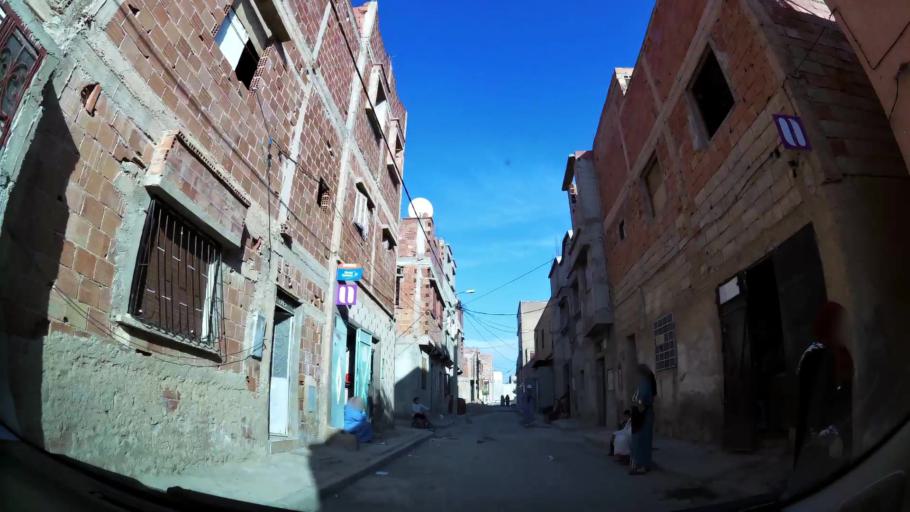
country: MA
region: Oriental
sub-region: Oujda-Angad
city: Oujda
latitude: 34.7116
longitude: -1.9026
